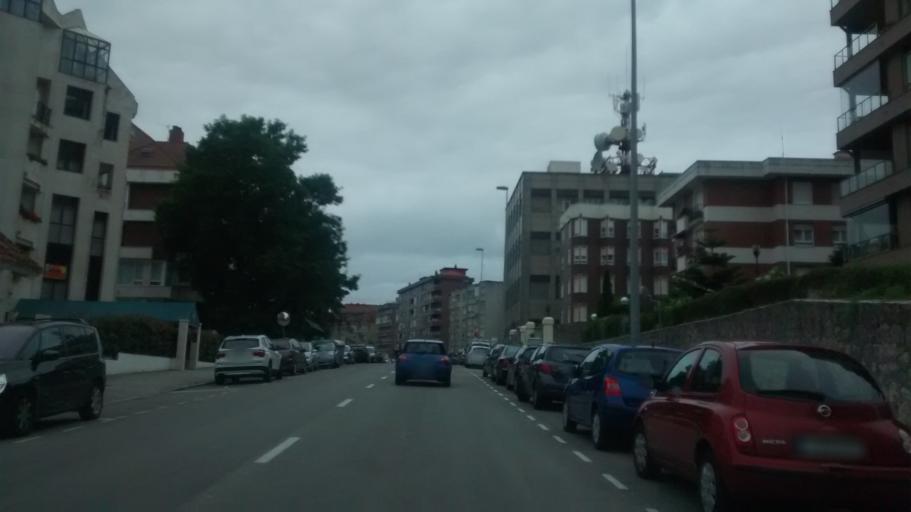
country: ES
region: Cantabria
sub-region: Provincia de Cantabria
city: Santander
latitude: 43.4683
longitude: -3.7902
